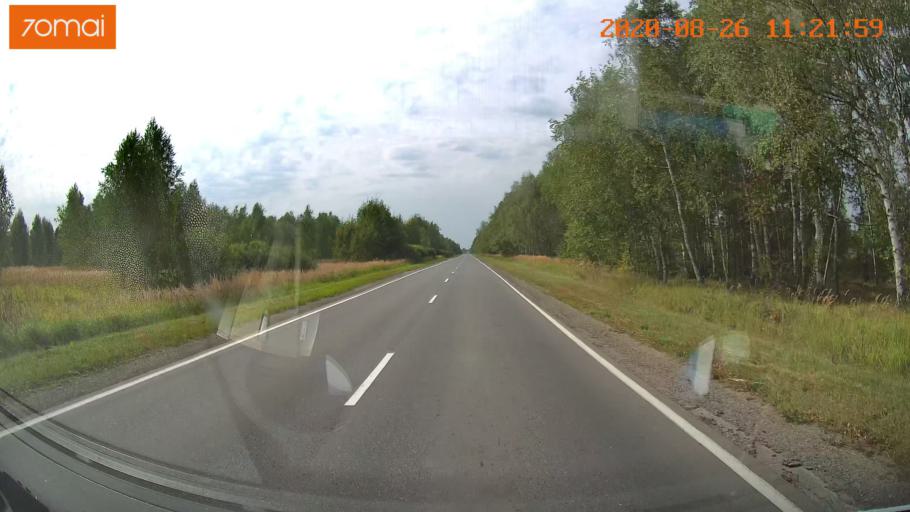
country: RU
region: Rjazan
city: Shilovo
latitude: 54.3695
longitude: 41.0353
